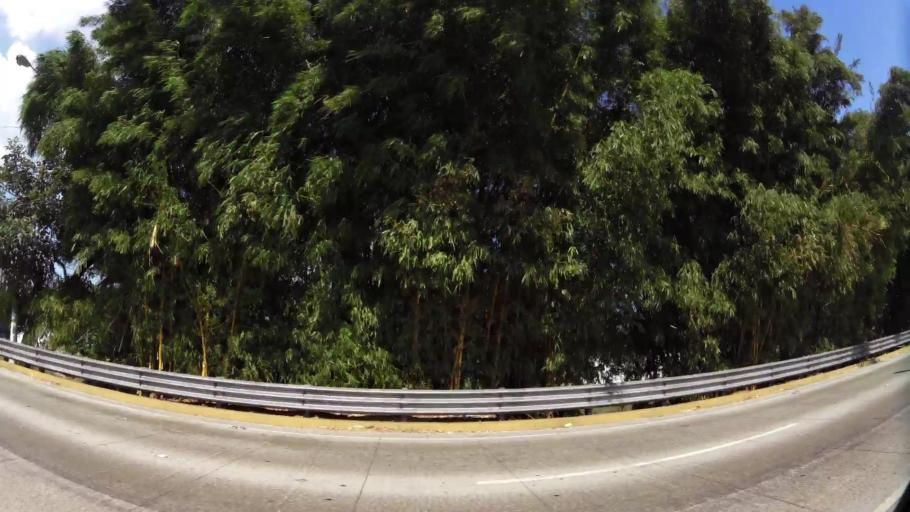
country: SV
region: La Libertad
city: Antiguo Cuscatlan
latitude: 13.6713
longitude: -89.2614
